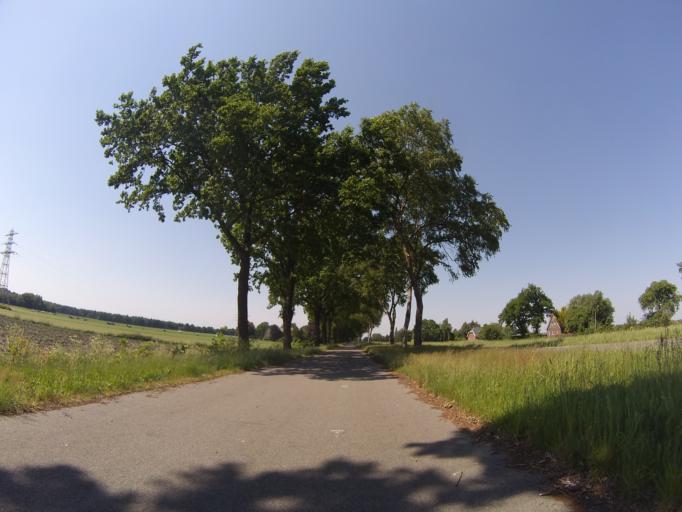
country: NL
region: Drenthe
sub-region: Gemeente Coevorden
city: Sleen
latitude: 52.7179
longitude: 6.8395
